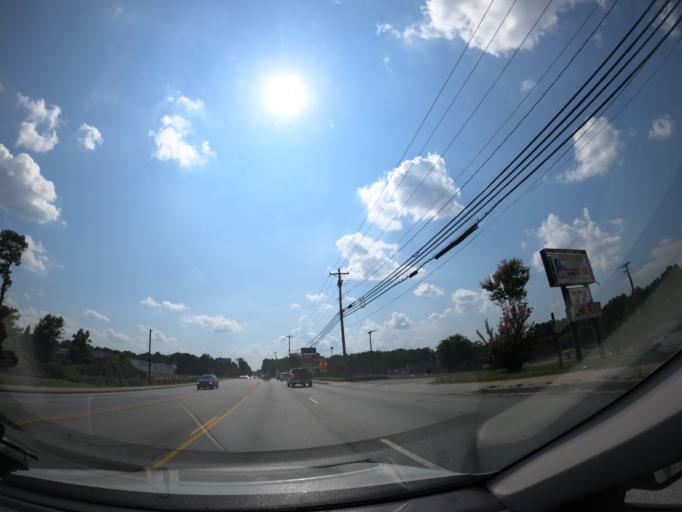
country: US
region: South Carolina
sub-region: Lexington County
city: Oak Grove
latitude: 33.9769
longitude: -81.1259
